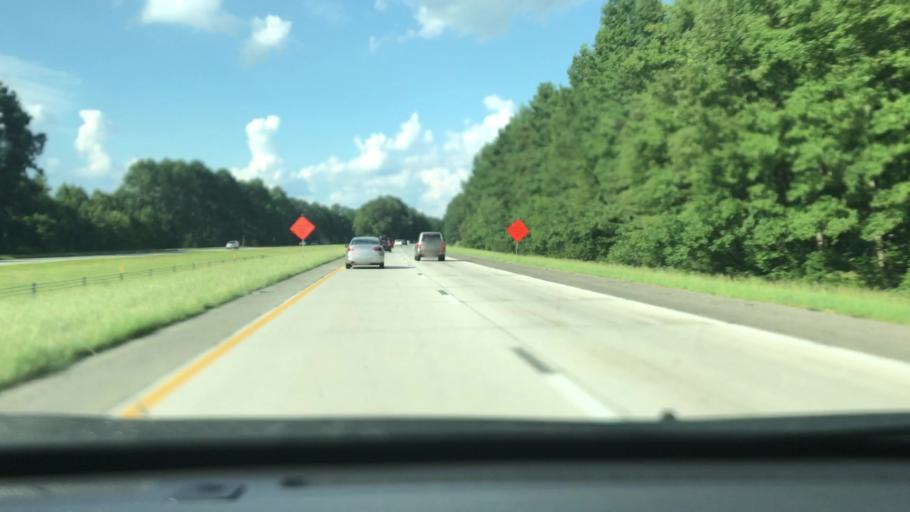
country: US
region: South Carolina
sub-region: Florence County
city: Timmonsville
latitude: 34.0903
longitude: -79.9328
